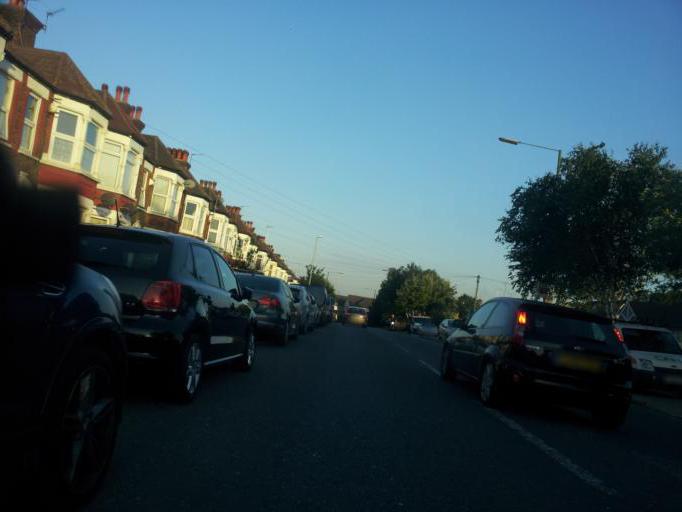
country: GB
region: England
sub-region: Kent
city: Dartford
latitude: 51.4522
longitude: 0.2105
